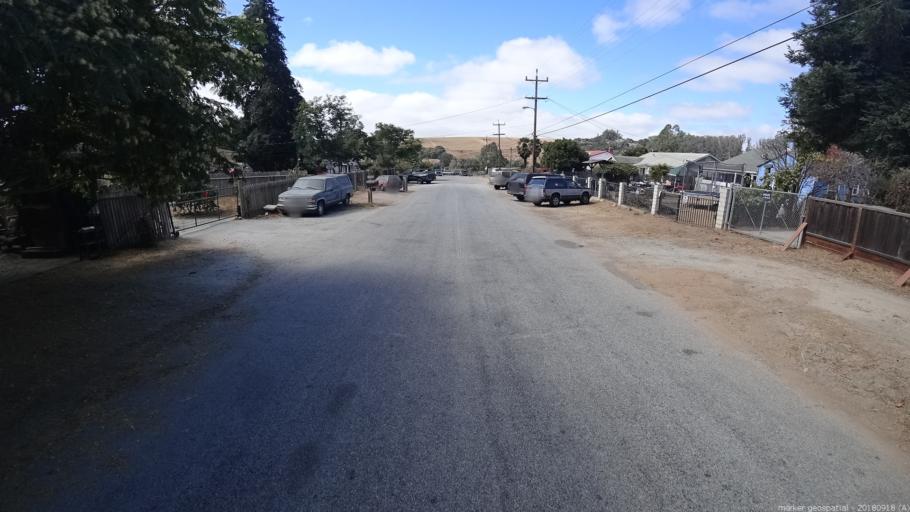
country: US
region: California
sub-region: Monterey County
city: Prunedale
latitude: 36.7742
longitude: -121.6672
